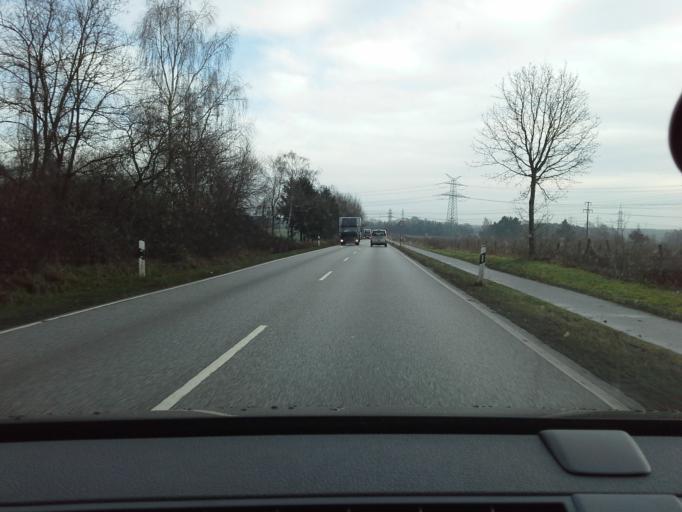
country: DE
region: Schleswig-Holstein
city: Ellerau
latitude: 53.7409
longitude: 9.9588
